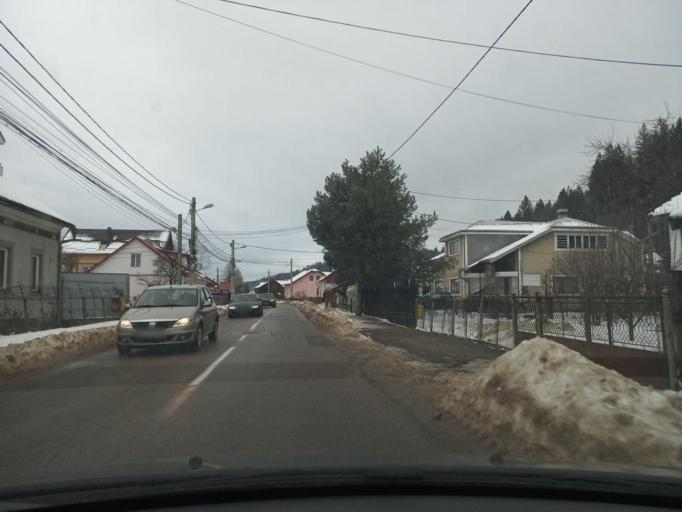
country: RO
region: Suceava
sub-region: Oras Gura Humorului
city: Gura Humorului
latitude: 47.5623
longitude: 25.8860
